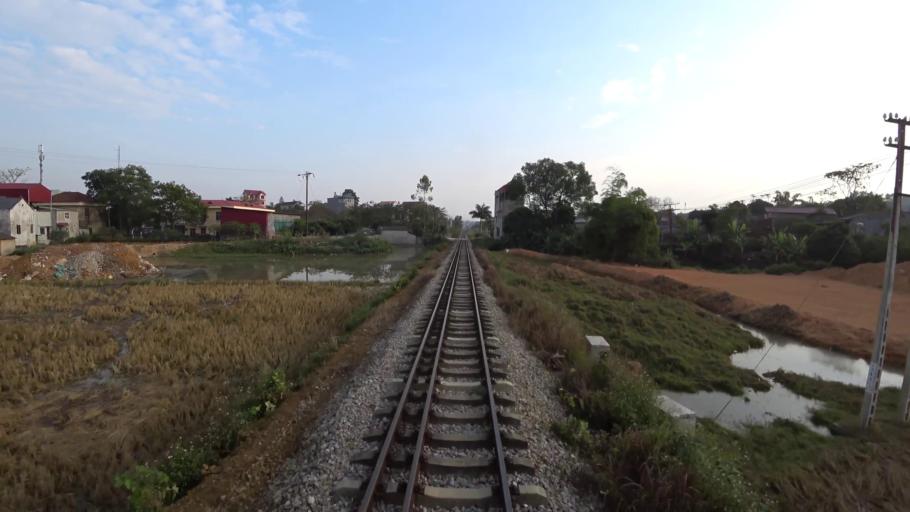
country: VN
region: Lang Son
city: Thi Tran Cao Loc
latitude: 21.8841
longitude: 106.7476
